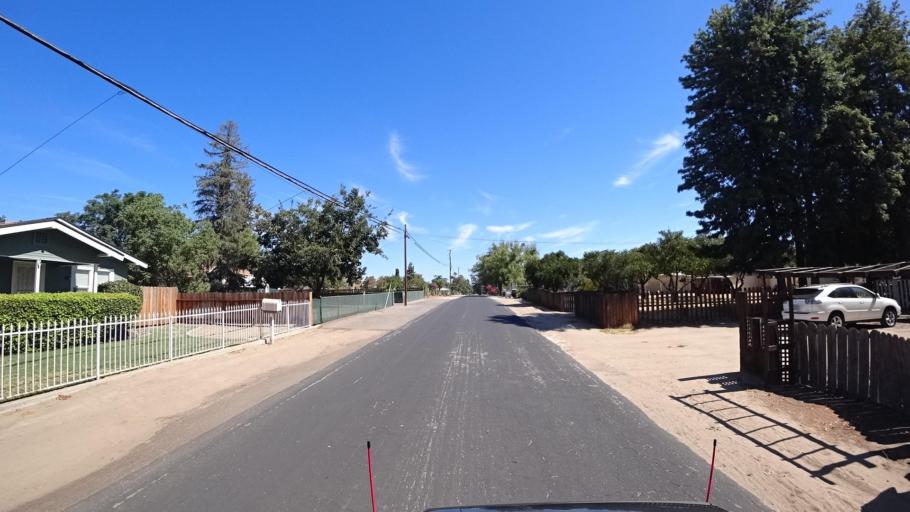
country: US
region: California
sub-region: Fresno County
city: Sunnyside
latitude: 36.7412
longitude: -119.7137
